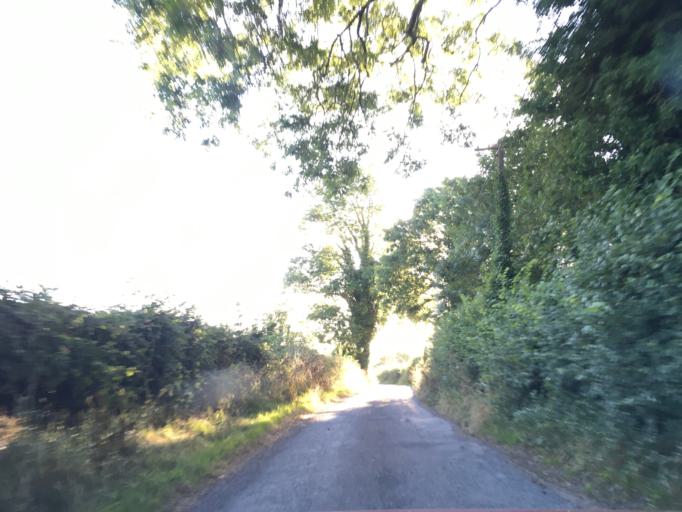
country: IE
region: Munster
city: Cashel
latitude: 52.4920
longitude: -7.9405
